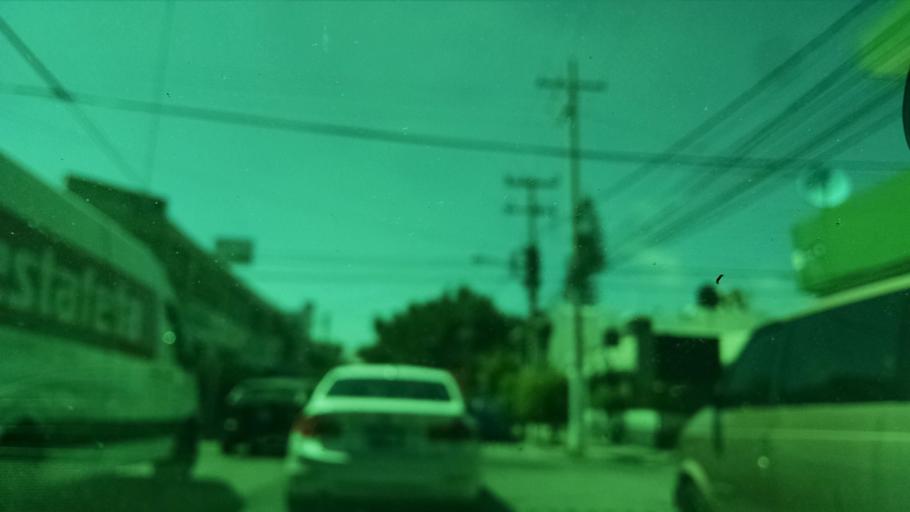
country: MX
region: Guanajuato
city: Leon
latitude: 21.1431
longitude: -101.6892
